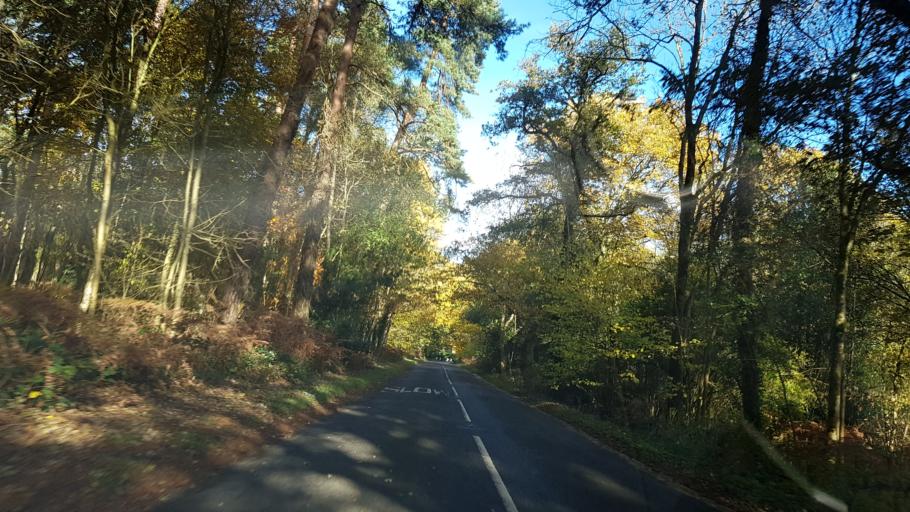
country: GB
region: England
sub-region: Surrey
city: Elstead
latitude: 51.1564
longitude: -0.7205
